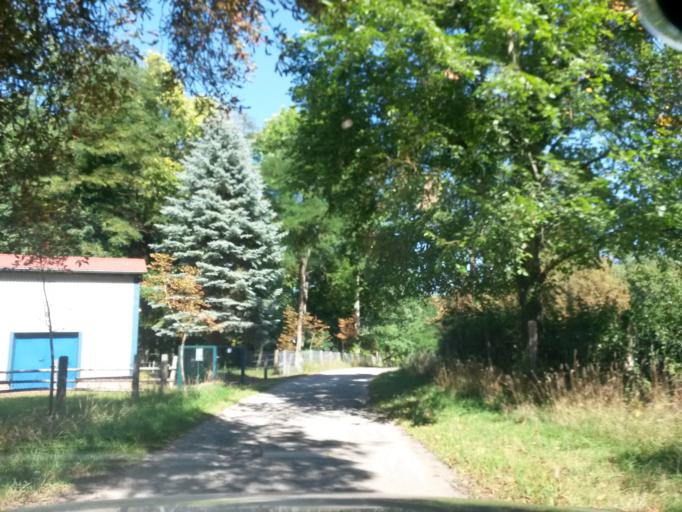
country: DE
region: Brandenburg
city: Templin
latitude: 53.2267
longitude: 13.4548
